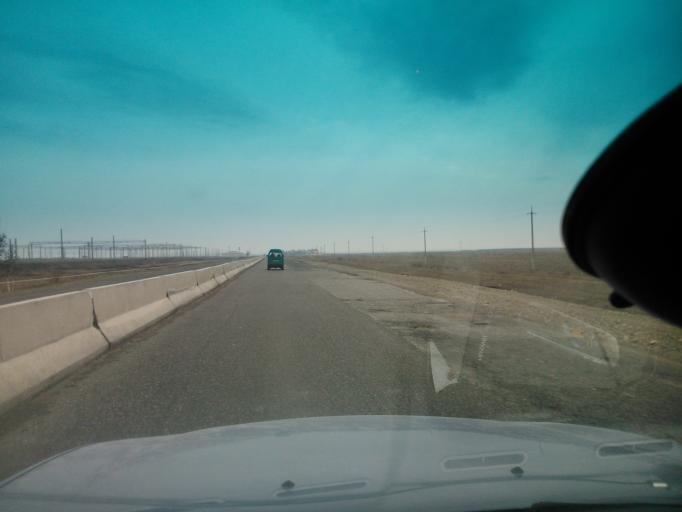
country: UZ
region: Sirdaryo
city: Yangiyer
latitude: 40.3723
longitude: 68.7991
